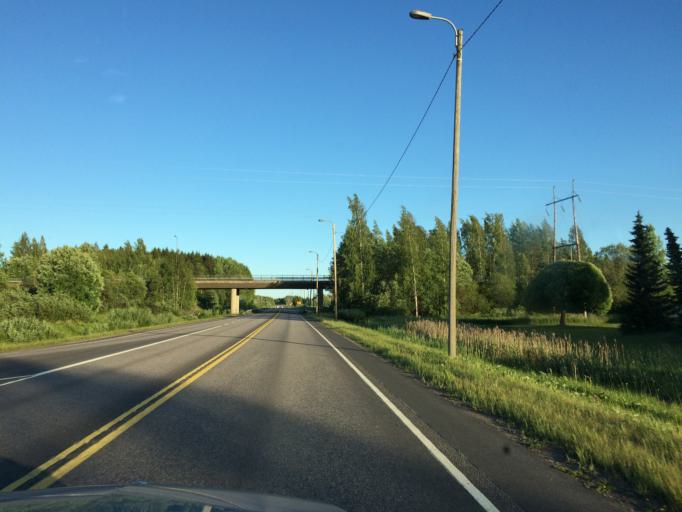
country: FI
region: Haeme
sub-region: Haemeenlinna
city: Tervakoski
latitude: 60.8191
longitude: 24.6391
